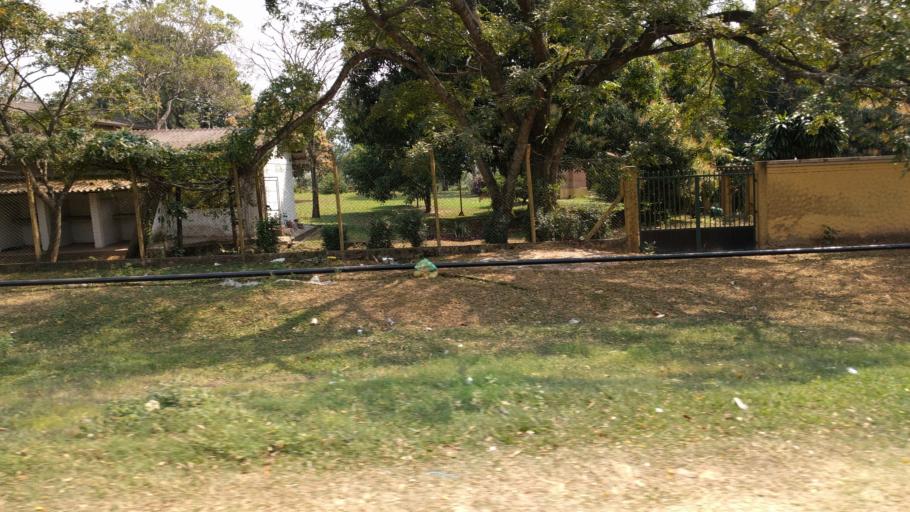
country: BO
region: Santa Cruz
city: Santa Rita
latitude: -17.9329
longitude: -63.3491
